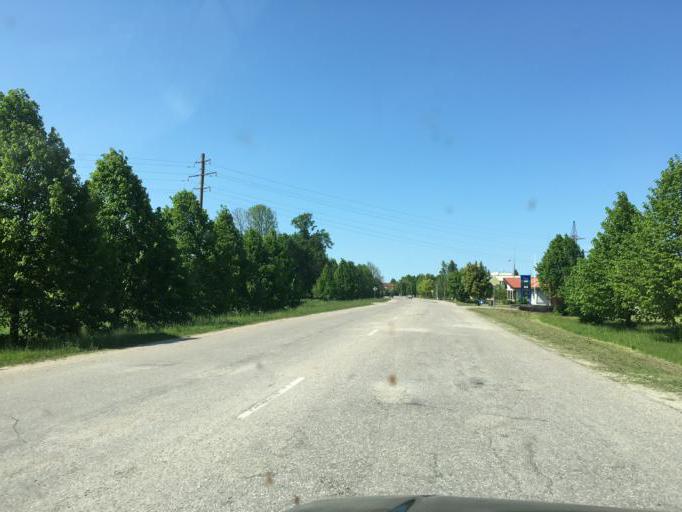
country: LV
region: Dundaga
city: Dundaga
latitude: 57.5021
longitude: 22.3521
